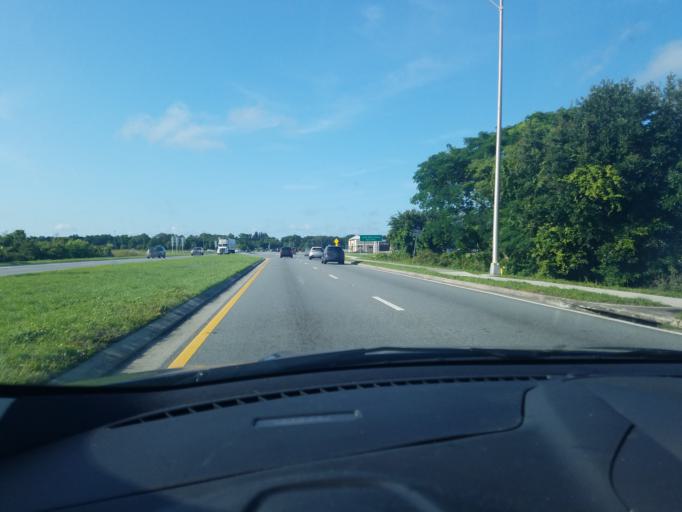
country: US
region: Florida
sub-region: Osceola County
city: Buenaventura Lakes
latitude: 28.3678
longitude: -81.3097
